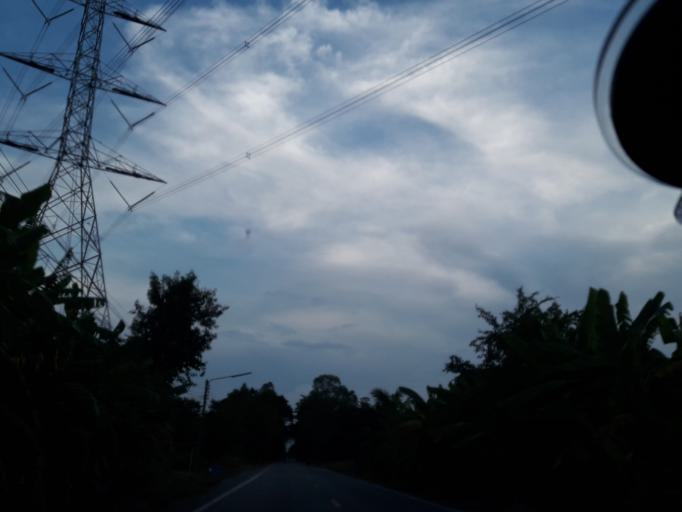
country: TH
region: Pathum Thani
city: Nong Suea
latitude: 14.1834
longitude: 100.8689
